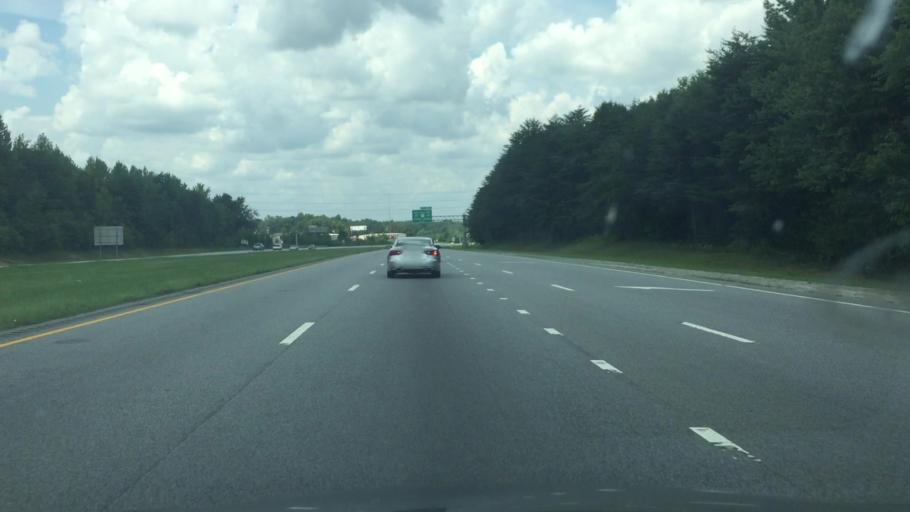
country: US
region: North Carolina
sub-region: Guilford County
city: Pleasant Garden
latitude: 35.9916
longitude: -79.8268
